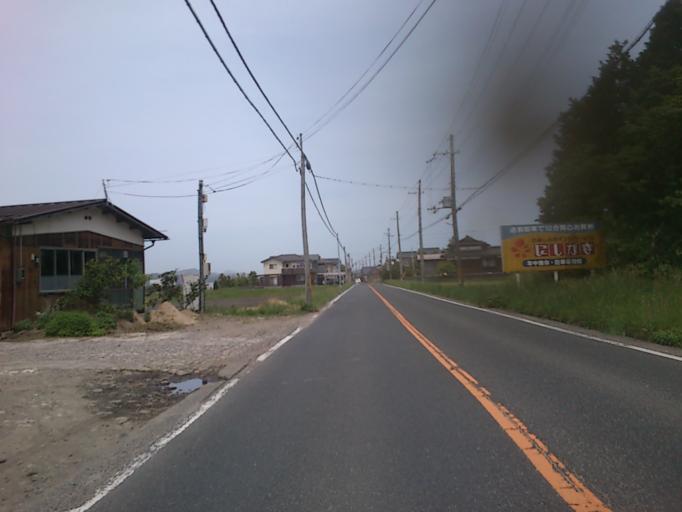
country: JP
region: Kyoto
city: Miyazu
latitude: 35.5948
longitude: 135.0970
